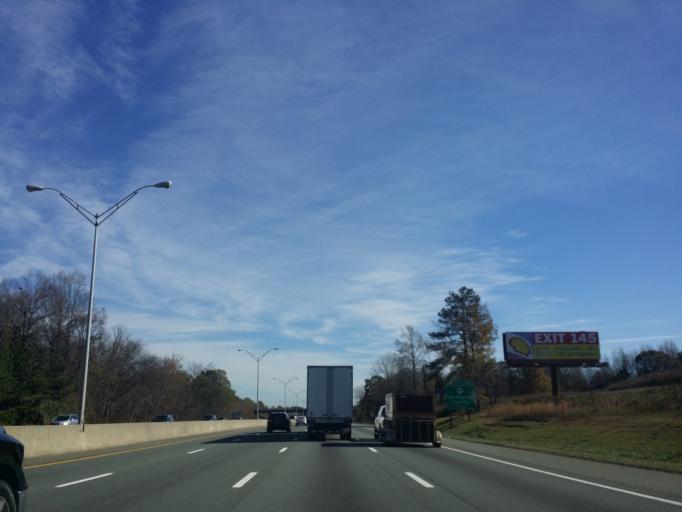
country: US
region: North Carolina
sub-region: Alamance County
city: Burlington
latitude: 36.0648
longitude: -79.4544
